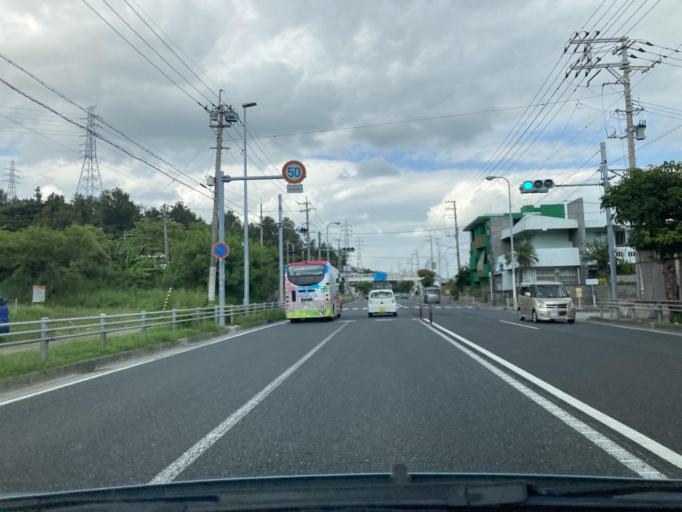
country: JP
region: Okinawa
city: Ginowan
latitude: 26.2472
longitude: 127.7819
